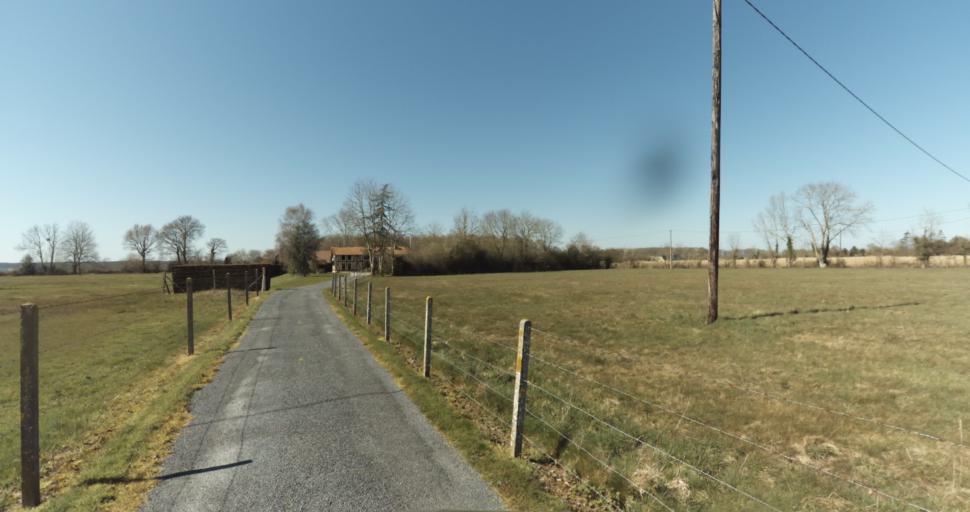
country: FR
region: Lower Normandy
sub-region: Departement du Calvados
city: Livarot
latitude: 49.0178
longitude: 0.1094
